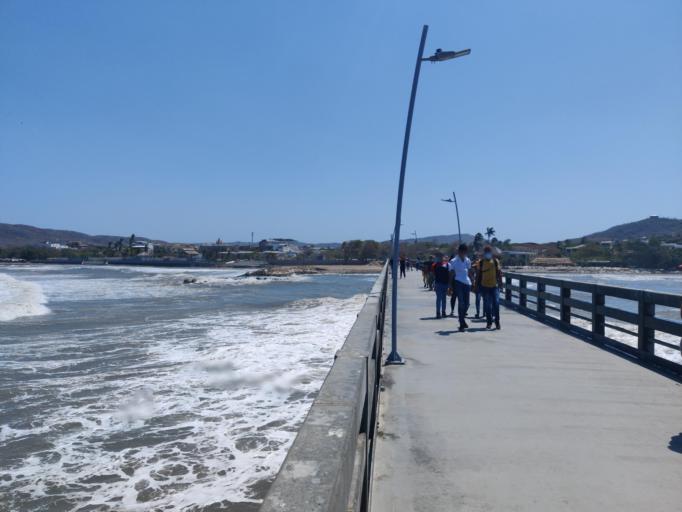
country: CO
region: Atlantico
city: Puerto Colombia
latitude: 10.9898
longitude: -74.9620
